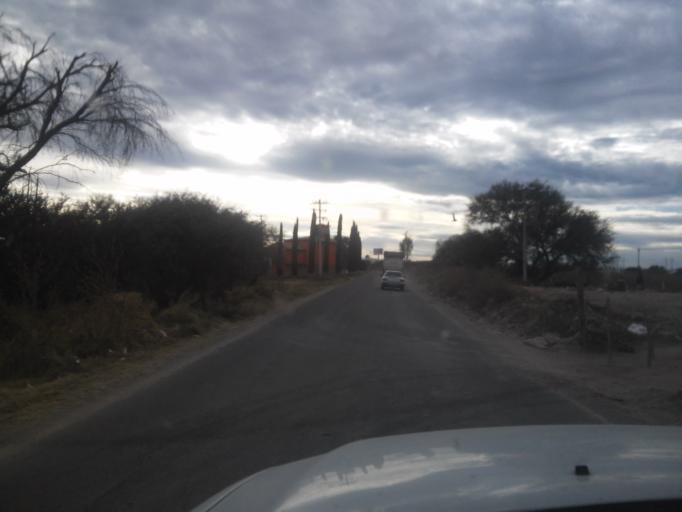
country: MX
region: Durango
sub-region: Durango
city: Jose Refugio Salcido
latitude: 24.0296
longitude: -104.5713
